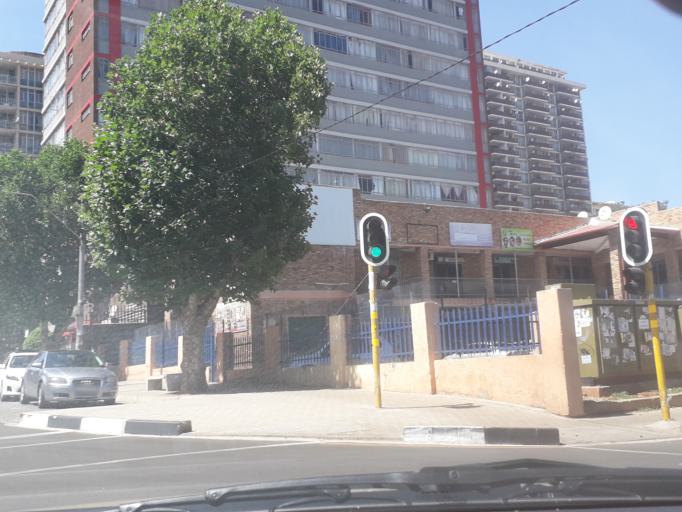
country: ZA
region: Gauteng
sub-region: City of Johannesburg Metropolitan Municipality
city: Johannesburg
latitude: -26.1854
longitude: 28.0538
